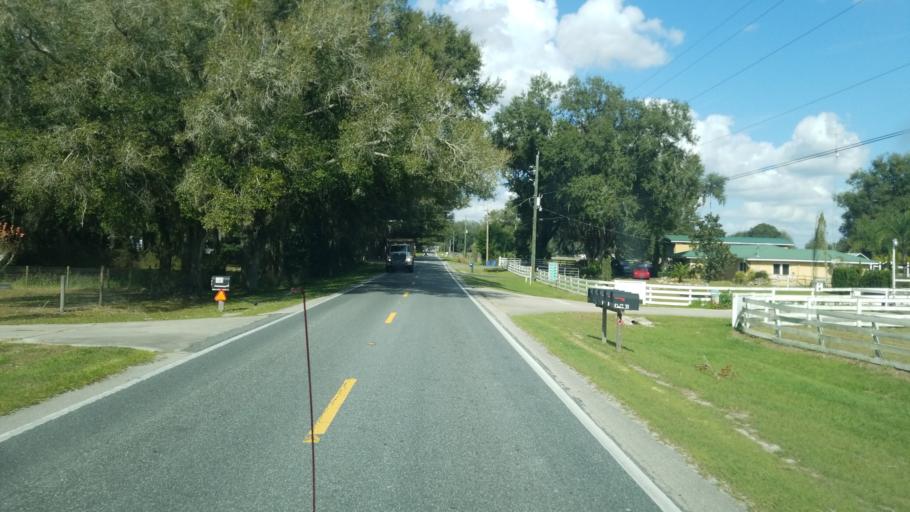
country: US
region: Florida
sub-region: Marion County
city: Belleview
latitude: 28.9736
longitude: -82.1199
